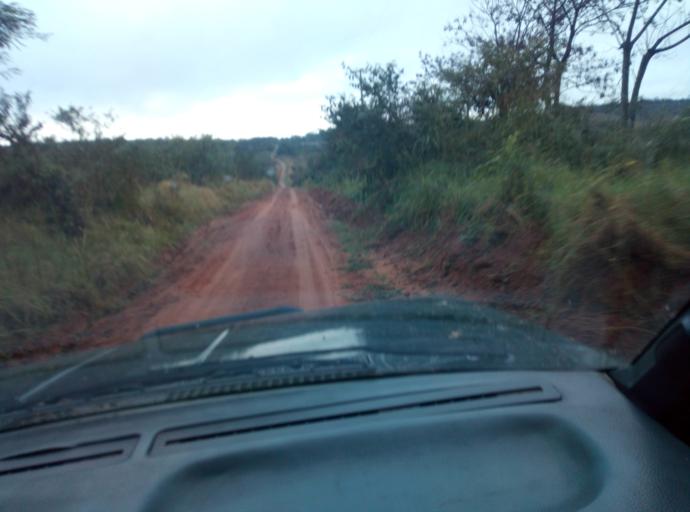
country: PY
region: Caaguazu
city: Carayao
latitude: -25.1903
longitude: -56.3473
